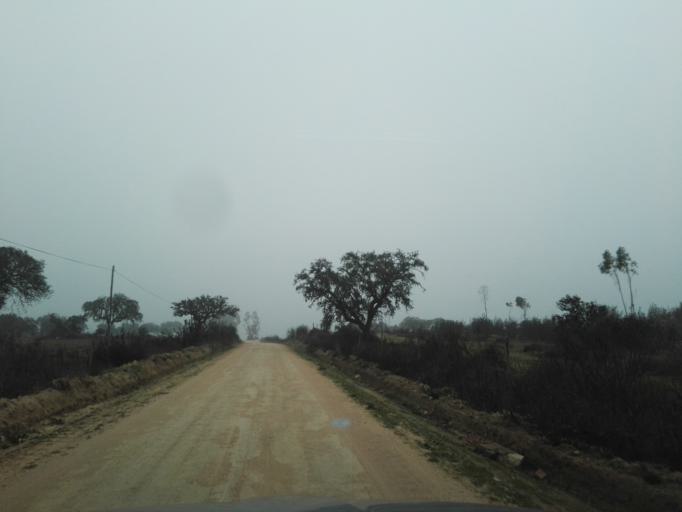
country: PT
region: Evora
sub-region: Montemor-O-Novo
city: Montemor-o-Novo
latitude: 38.7842
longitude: -8.2263
